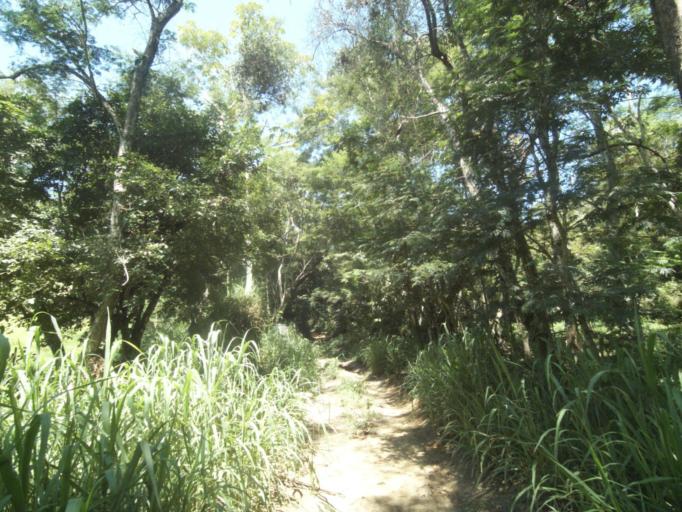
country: BR
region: Rio de Janeiro
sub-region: Sao Goncalo
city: Sao Goncalo
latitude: -22.9255
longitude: -42.9889
